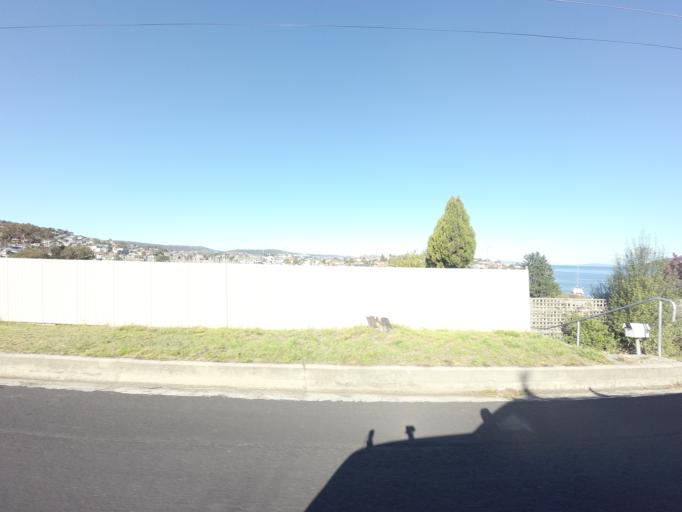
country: AU
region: Tasmania
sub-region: Clarence
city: Bellerive
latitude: -42.8716
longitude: 147.3614
